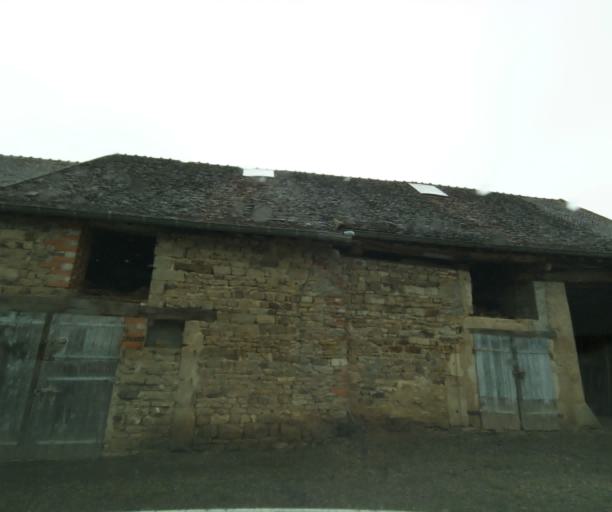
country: FR
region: Bourgogne
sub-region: Departement de Saone-et-Loire
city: Ciry-le-Noble
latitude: 46.5394
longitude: 4.3580
